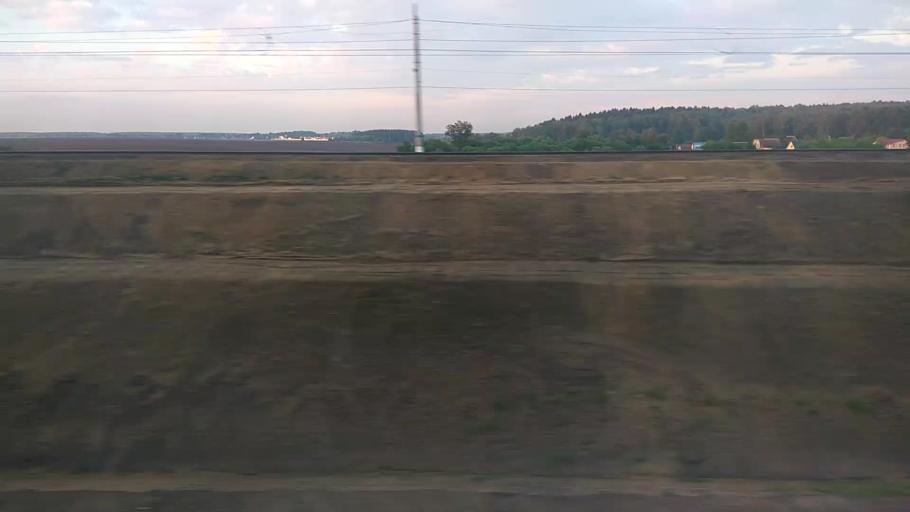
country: RU
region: Moskovskaya
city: Barybino
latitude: 55.2879
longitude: 37.8875
